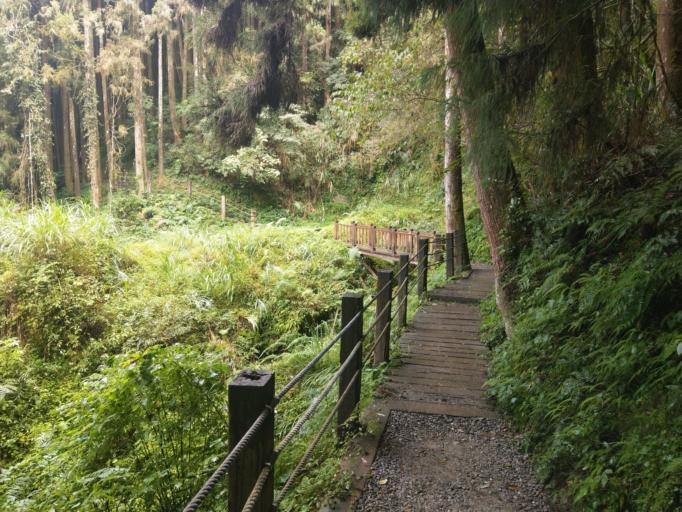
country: TW
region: Taiwan
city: Lugu
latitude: 23.6328
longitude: 120.7908
